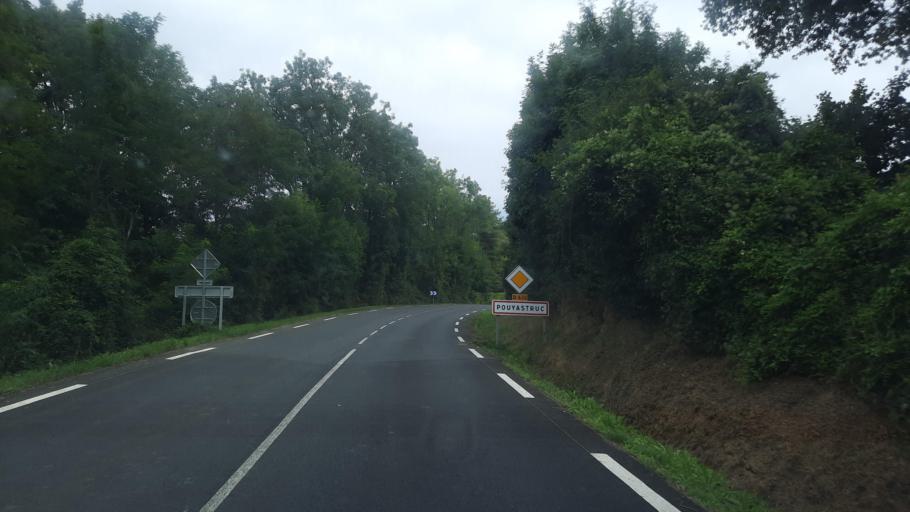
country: FR
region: Midi-Pyrenees
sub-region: Departement des Hautes-Pyrenees
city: Orleix
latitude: 43.2636
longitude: 0.1539
